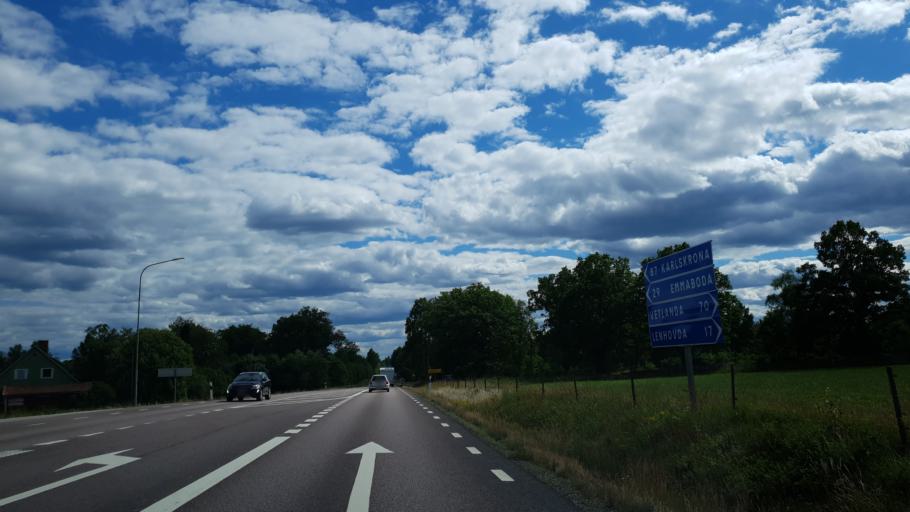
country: SE
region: Kronoberg
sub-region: Lessebo Kommun
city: Lessebo
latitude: 56.8582
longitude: 15.3880
